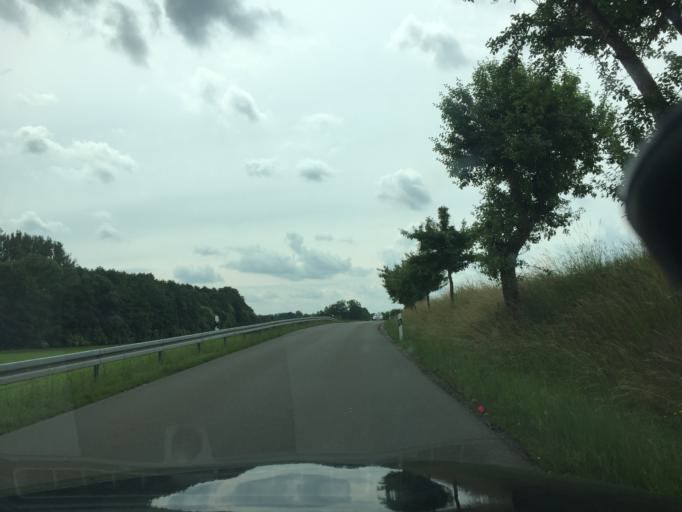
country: DE
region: Thuringia
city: Schmolln
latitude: 50.8848
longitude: 12.3364
